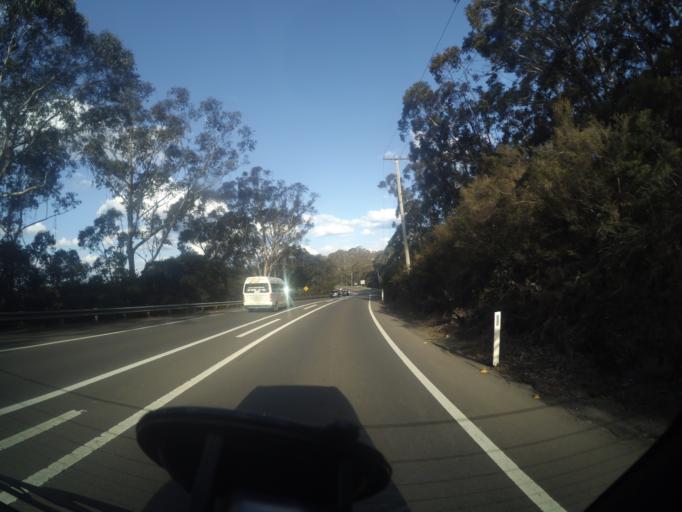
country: AU
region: New South Wales
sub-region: Blue Mountains Municipality
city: Katoomba
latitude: -33.7046
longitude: 150.2921
